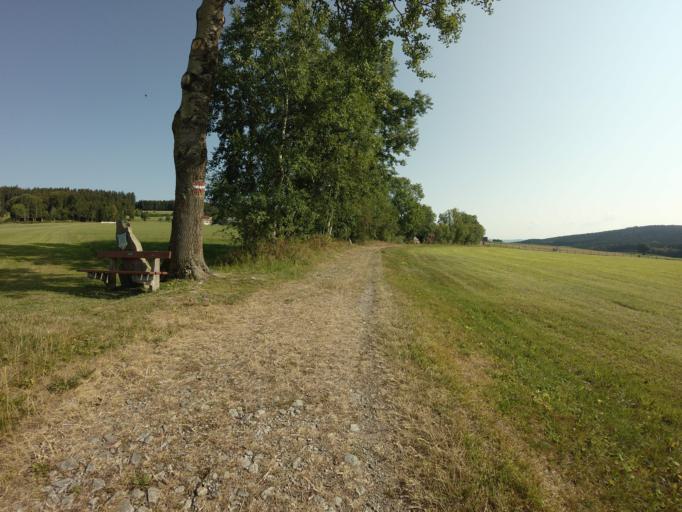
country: AT
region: Upper Austria
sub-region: Politischer Bezirk Urfahr-Umgebung
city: Bad Leonfelden
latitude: 48.5428
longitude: 14.3159
